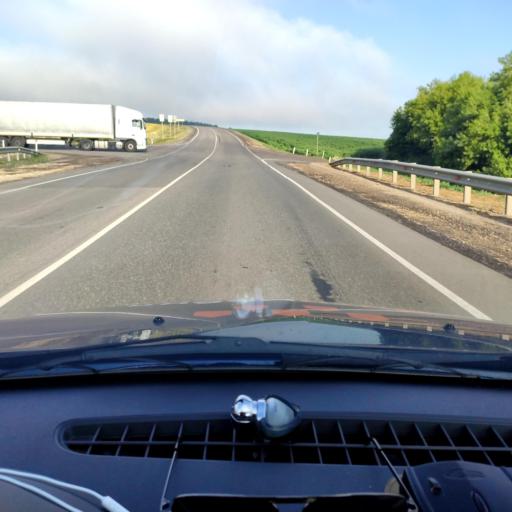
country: RU
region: Orjol
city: Livny
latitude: 52.4477
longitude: 37.4655
